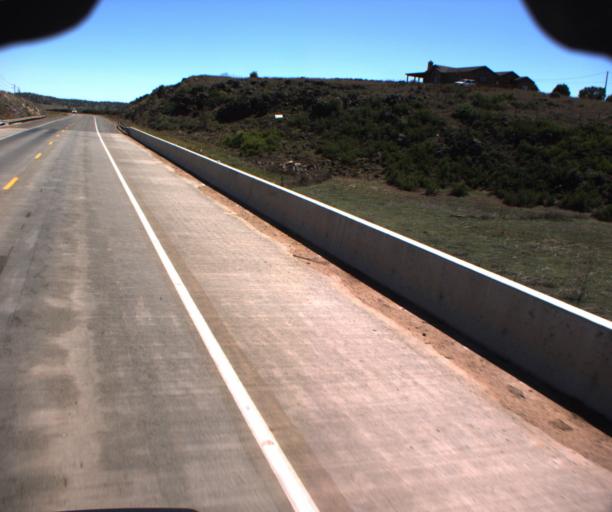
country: US
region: Arizona
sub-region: Yavapai County
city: Paulden
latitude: 34.8703
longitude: -112.4699
